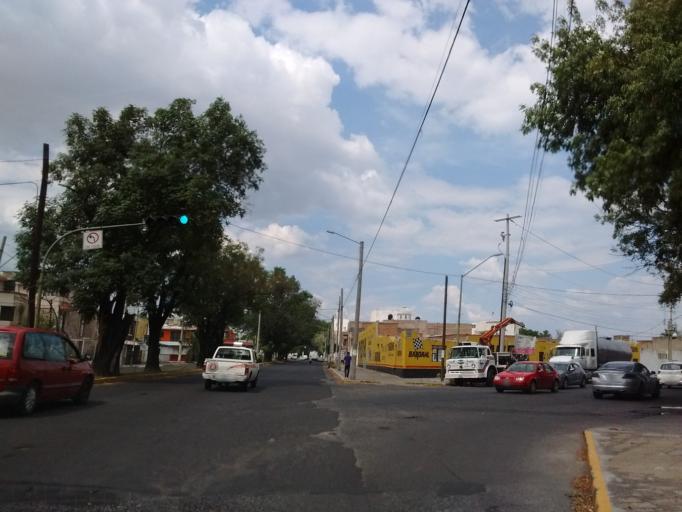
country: MX
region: Jalisco
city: Tlaquepaque
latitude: 20.6519
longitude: -103.3287
